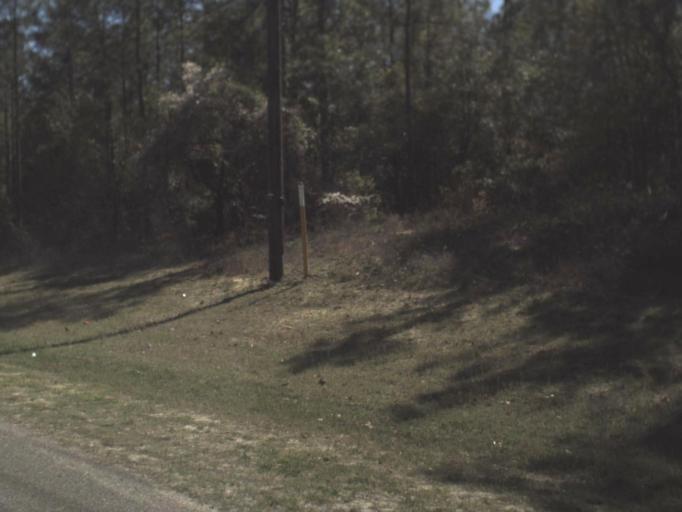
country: US
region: Florida
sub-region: Leon County
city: Tallahassee
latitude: 30.3857
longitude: -84.3108
